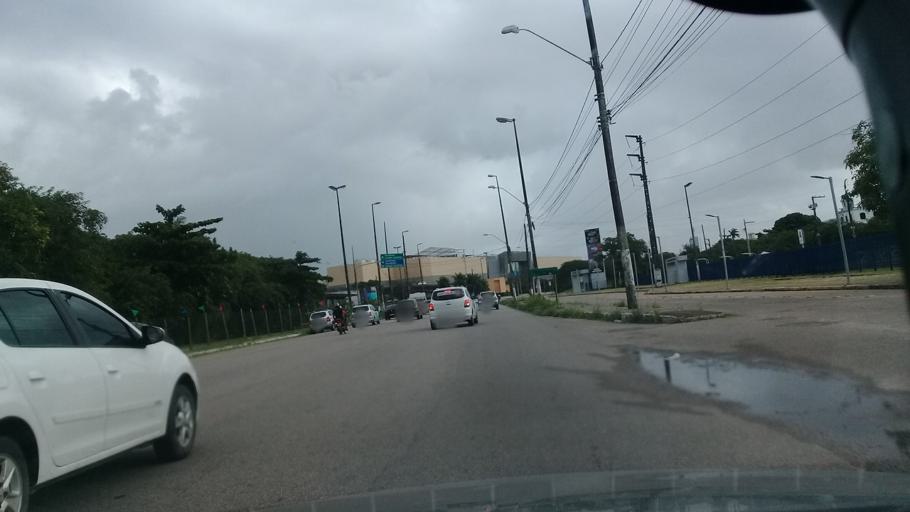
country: BR
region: Pernambuco
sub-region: Recife
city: Recife
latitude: -8.0343
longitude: -34.8696
